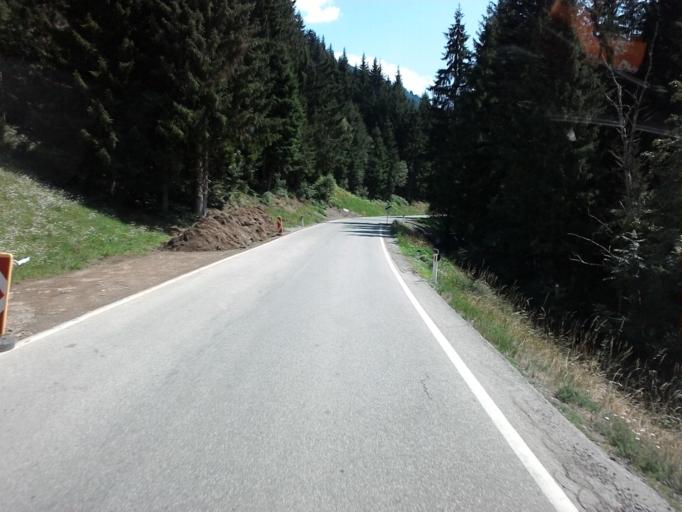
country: AT
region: Tyrol
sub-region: Politischer Bezirk Lienz
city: Untertilliach
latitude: 46.7046
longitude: 12.6949
